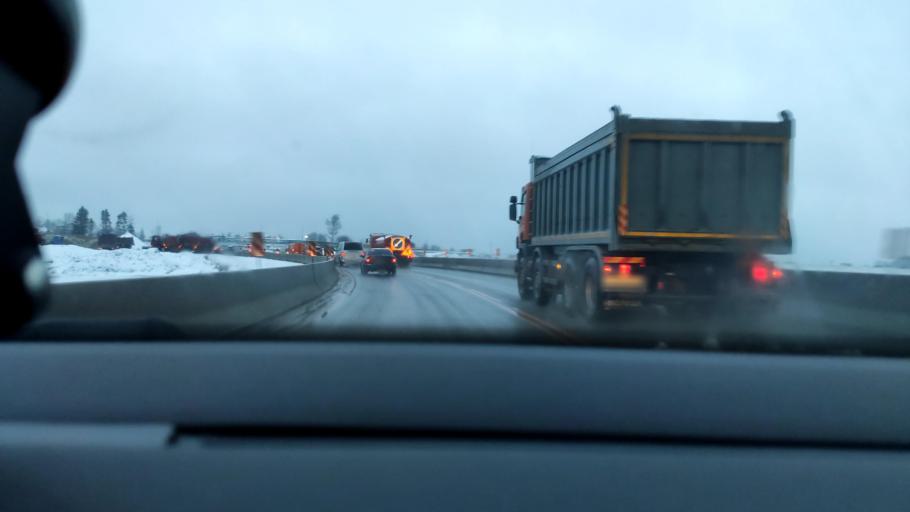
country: RU
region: Moskovskaya
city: Kubinka
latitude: 55.5688
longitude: 36.7013
